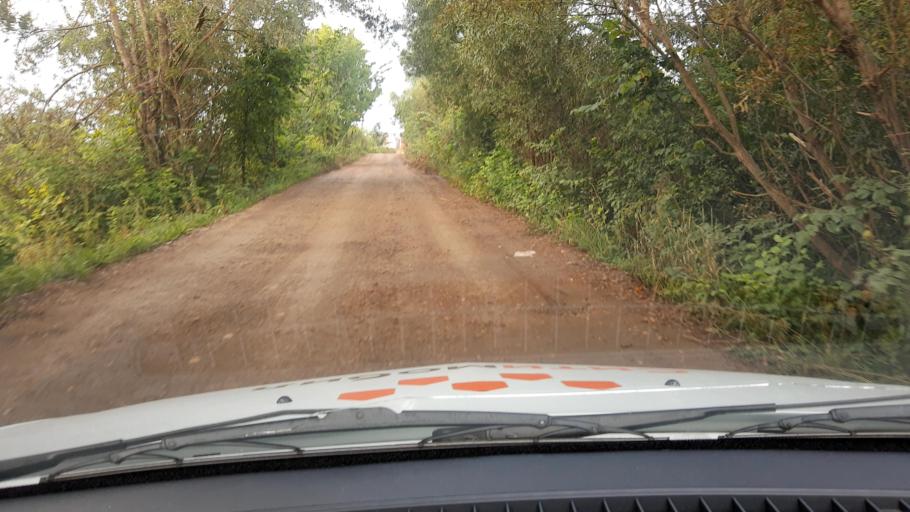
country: RU
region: Bashkortostan
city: Kabakovo
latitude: 54.7003
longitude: 56.1347
